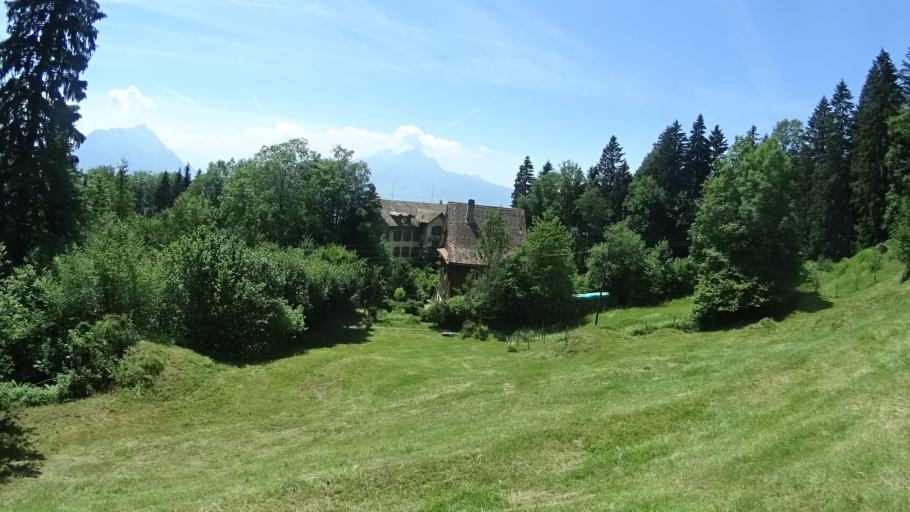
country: CH
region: Lucerne
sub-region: Lucerne-Land District
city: Vitznau
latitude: 47.0265
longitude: 8.4827
